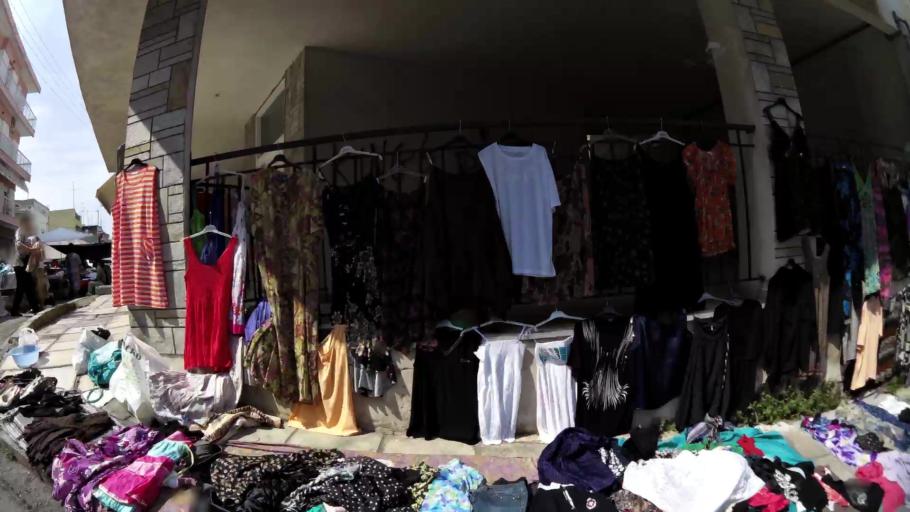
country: GR
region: Central Macedonia
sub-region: Nomos Thessalonikis
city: Thessaloniki
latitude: 40.6484
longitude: 22.9386
